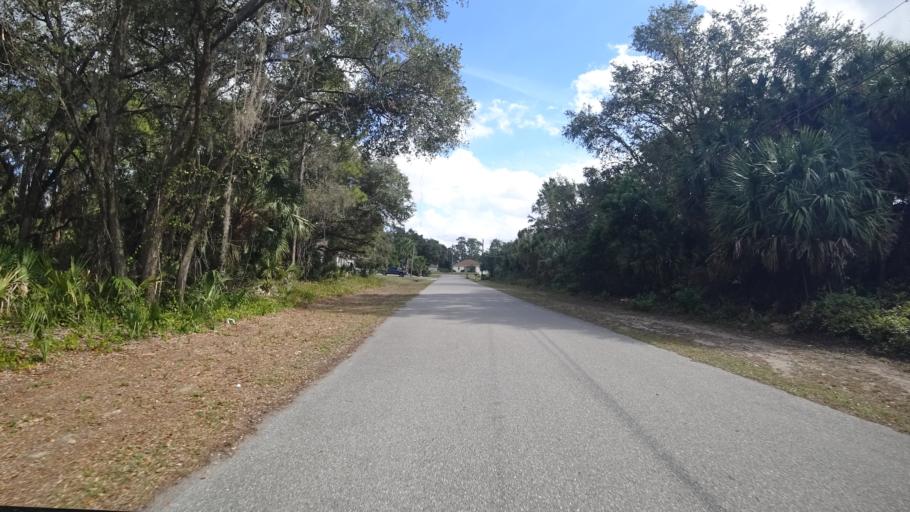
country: US
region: Florida
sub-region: Charlotte County
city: Port Charlotte
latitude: 27.0374
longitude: -82.1350
